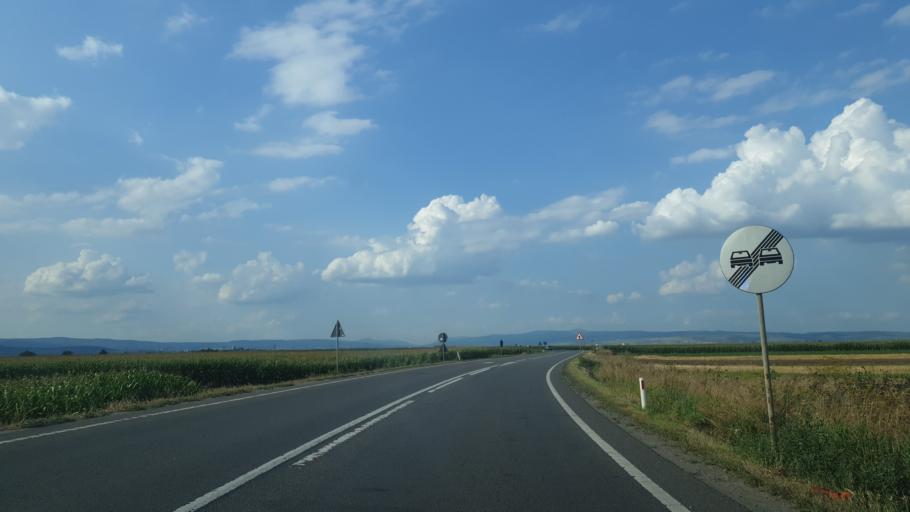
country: RO
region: Covasna
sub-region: Comuna Chichis
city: Chichis
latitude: 45.7818
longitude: 25.8062
